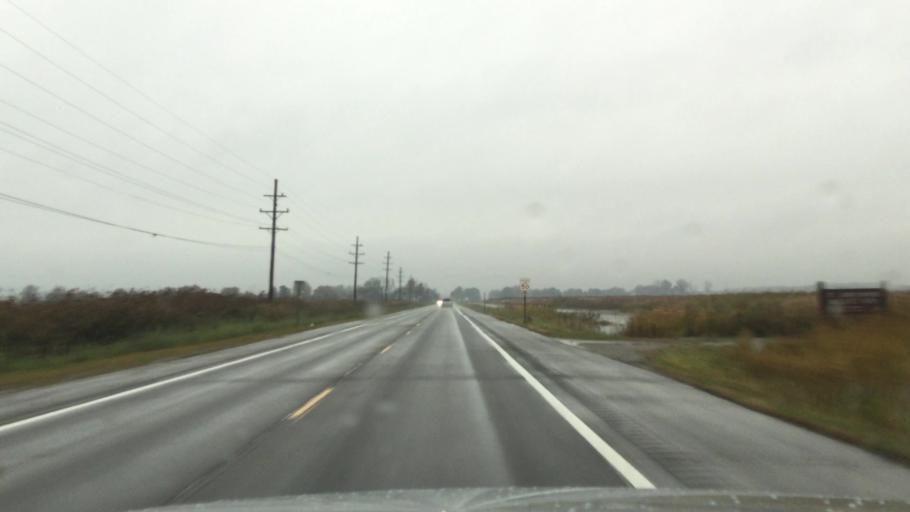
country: US
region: Michigan
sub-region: Saint Clair County
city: Pearl Beach
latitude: 42.6474
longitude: -82.6178
